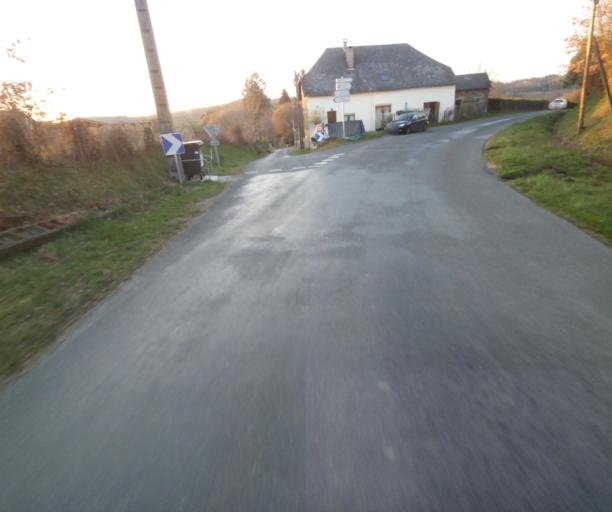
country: FR
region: Limousin
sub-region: Departement de la Correze
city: Saint-Clement
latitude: 45.3645
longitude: 1.6216
